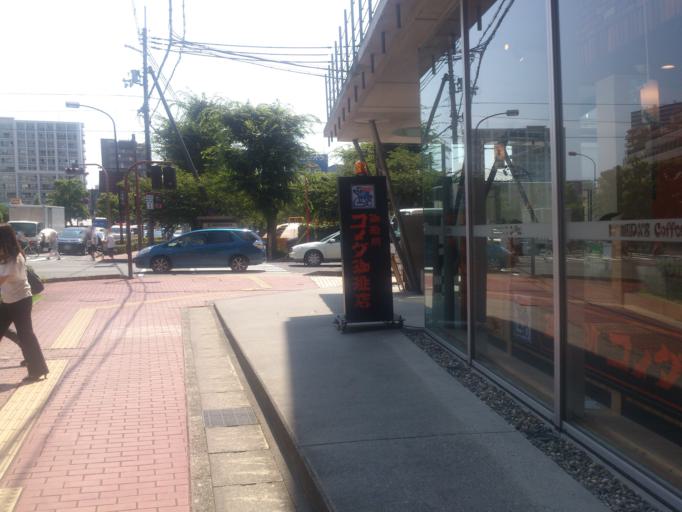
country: JP
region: Shiga Prefecture
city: Otsu-shi
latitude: 35.0038
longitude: 135.8808
